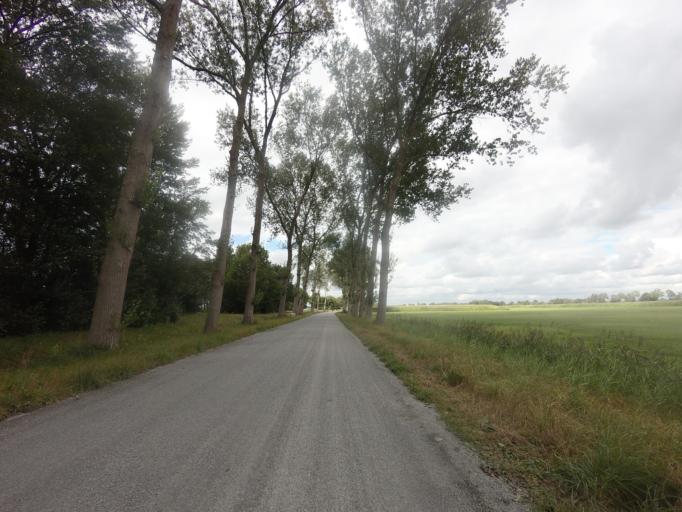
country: NL
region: Drenthe
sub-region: Gemeente Meppel
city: Meppel
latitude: 52.7123
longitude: 6.1764
